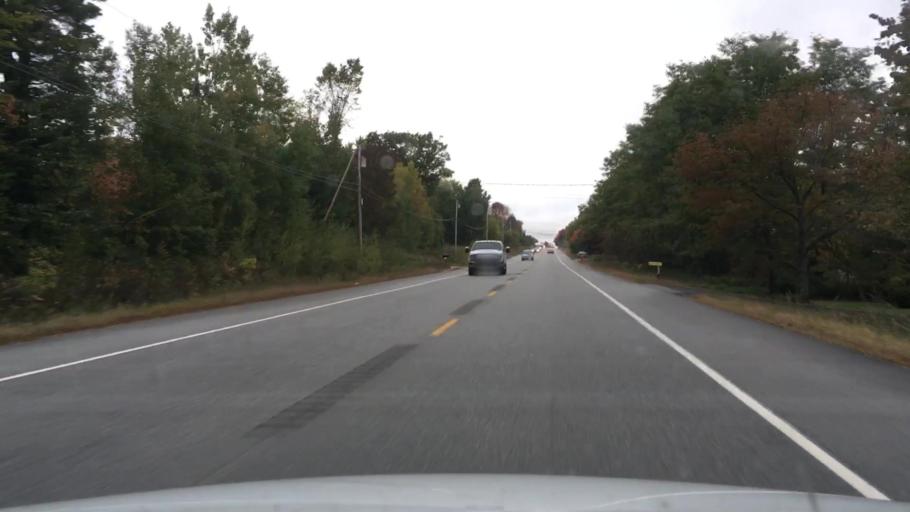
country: US
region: Maine
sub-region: Androscoggin County
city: Mechanic Falls
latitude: 44.1090
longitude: -70.4382
